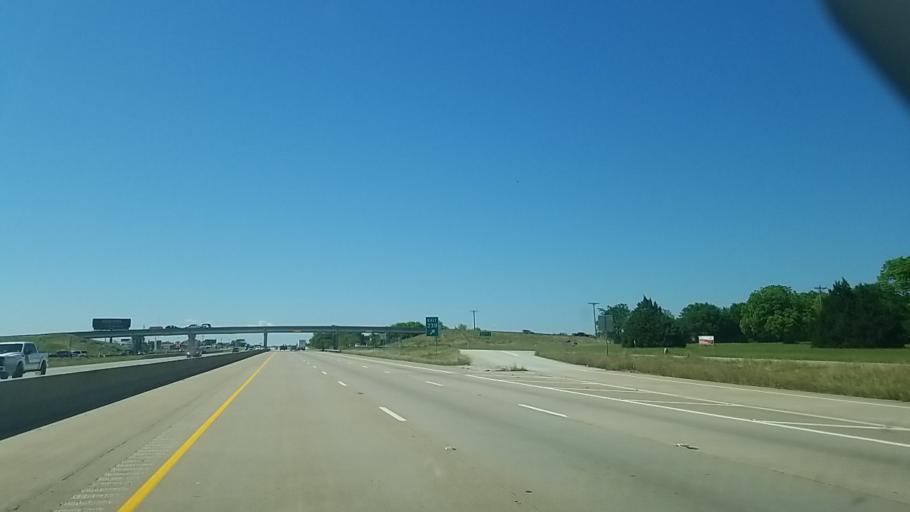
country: US
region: Texas
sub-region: Navarro County
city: Corsicana
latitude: 32.2151
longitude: -96.4815
